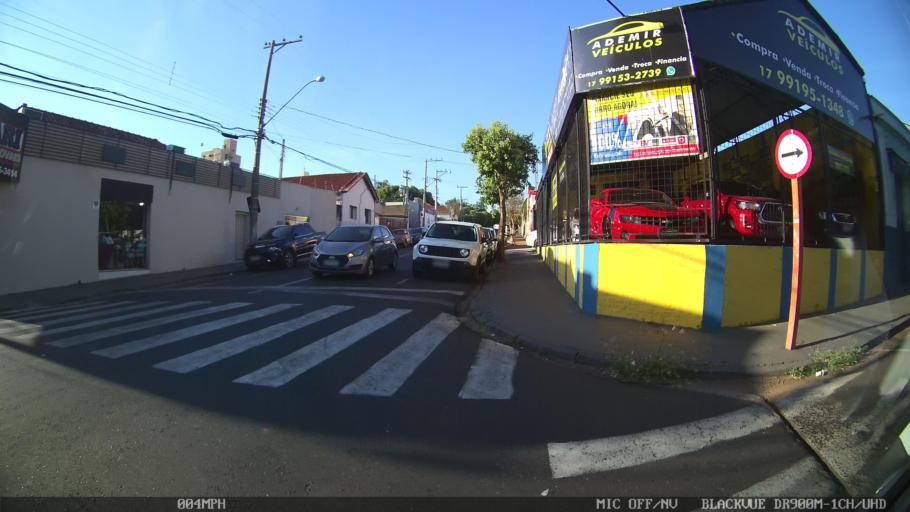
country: BR
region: Sao Paulo
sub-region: Sao Jose Do Rio Preto
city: Sao Jose do Rio Preto
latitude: -20.8053
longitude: -49.3729
